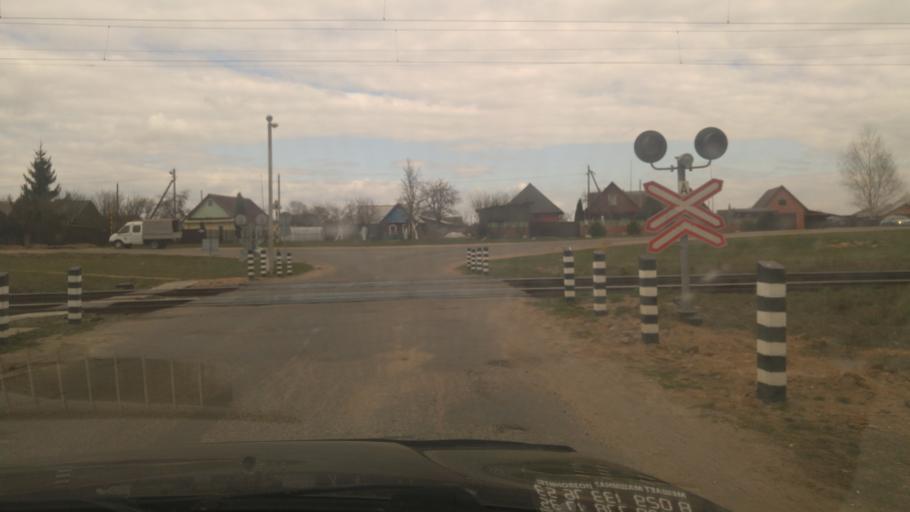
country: BY
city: Michanovichi
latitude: 53.6717
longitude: 27.7498
